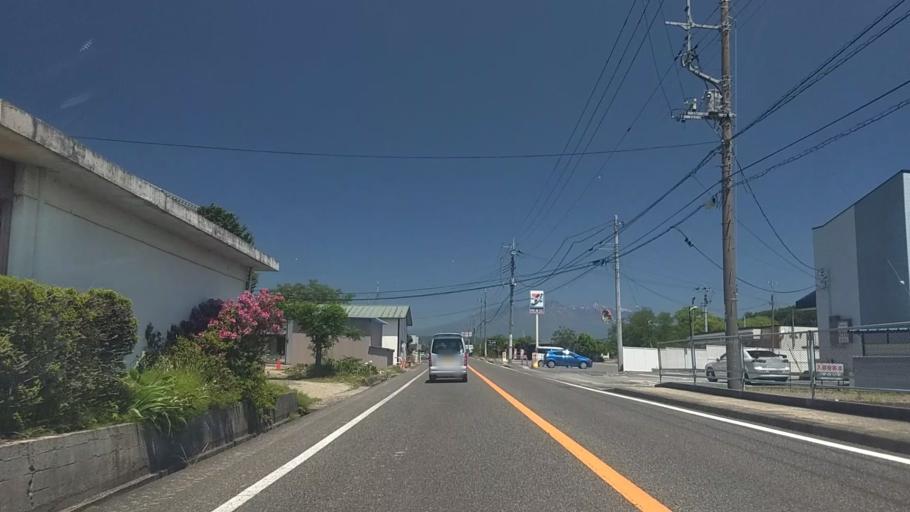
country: JP
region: Yamanashi
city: Nirasaki
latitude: 35.7414
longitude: 138.4429
